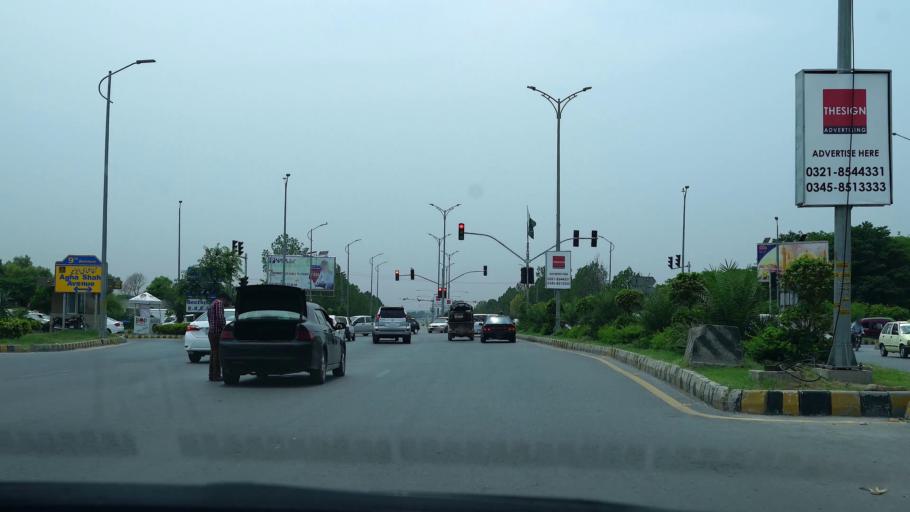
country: PK
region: Islamabad
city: Islamabad
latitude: 33.7045
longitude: 73.0460
